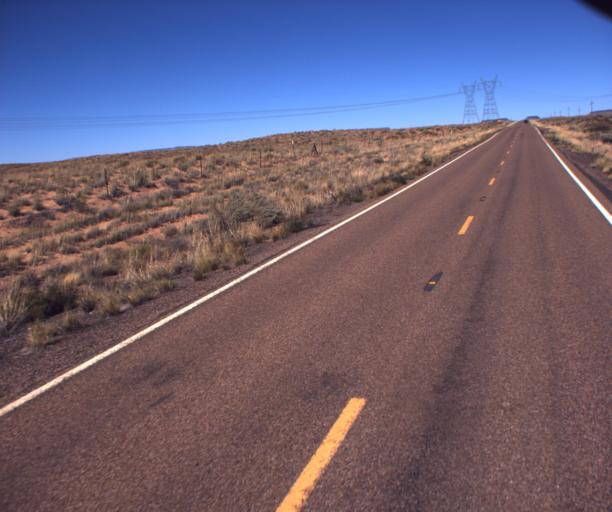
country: US
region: Arizona
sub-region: Navajo County
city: Holbrook
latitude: 35.1573
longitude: -110.0832
